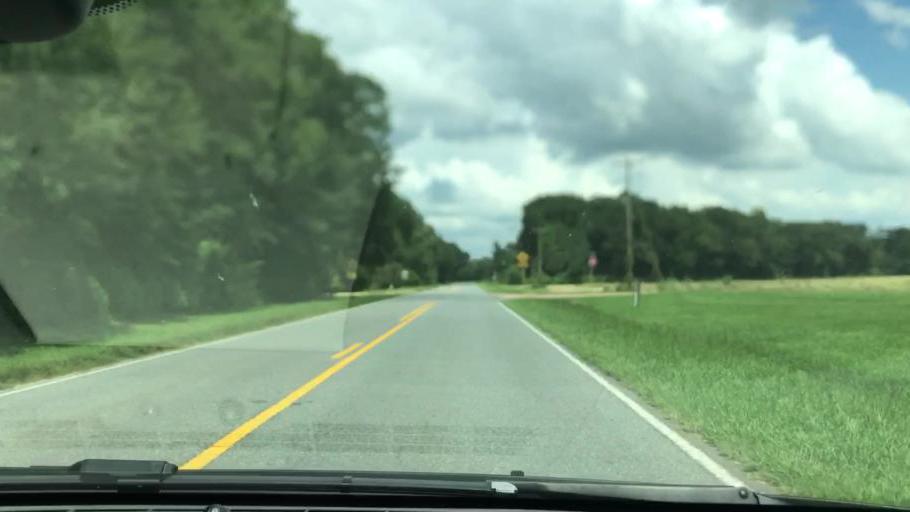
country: US
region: Florida
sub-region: Jackson County
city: Malone
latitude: 30.9040
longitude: -85.1295
